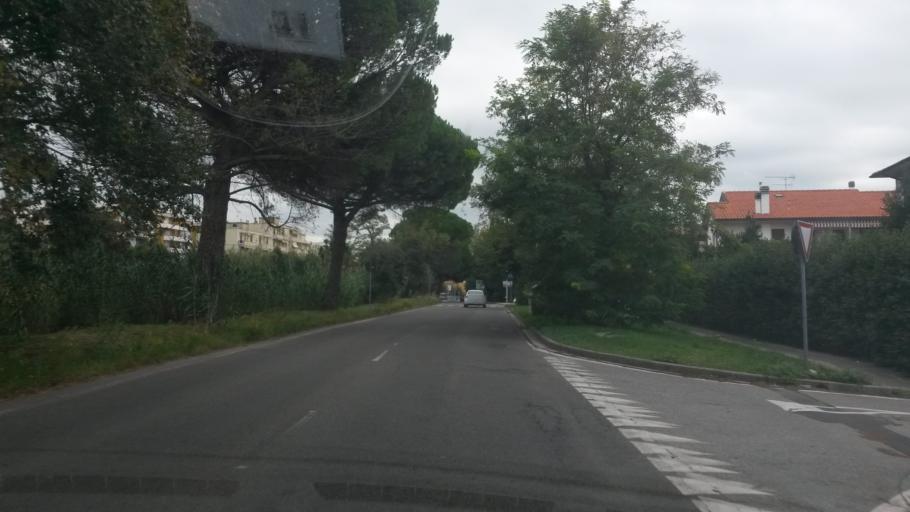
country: IT
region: Tuscany
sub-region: Provincia di Livorno
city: Rosignano Solvay-Castiglioncello
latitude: 43.3996
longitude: 10.4394
